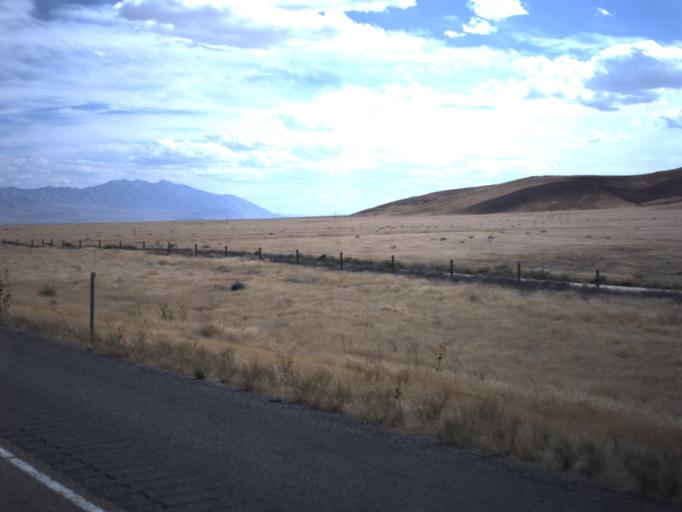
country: US
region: Utah
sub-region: Tooele County
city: Grantsville
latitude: 40.8087
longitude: -112.8655
